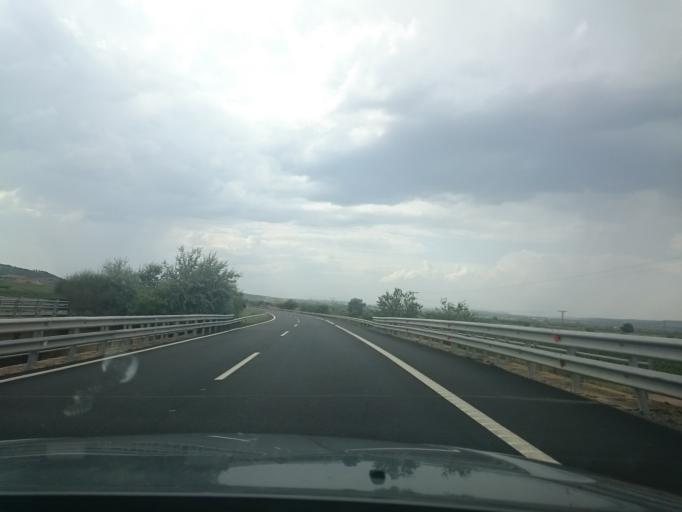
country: ES
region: La Rioja
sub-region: Provincia de La Rioja
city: Aldeanueva de Ebro
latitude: 42.2469
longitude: -1.9036
